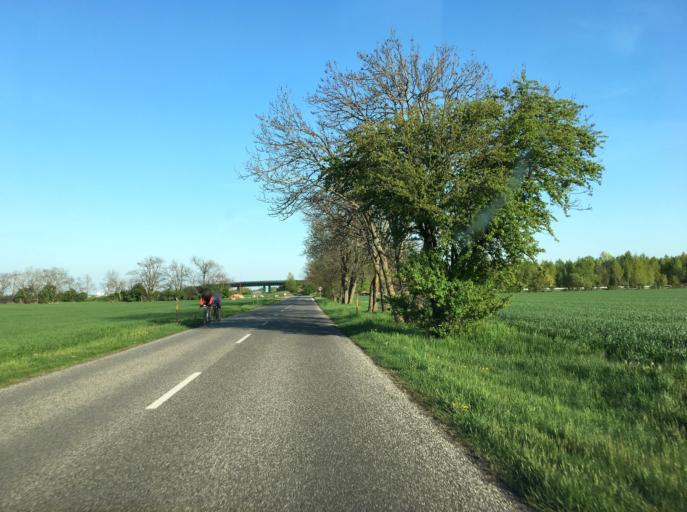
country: AT
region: Burgenland
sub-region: Politischer Bezirk Neusiedl am See
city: Kittsee
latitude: 48.0737
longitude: 17.0908
